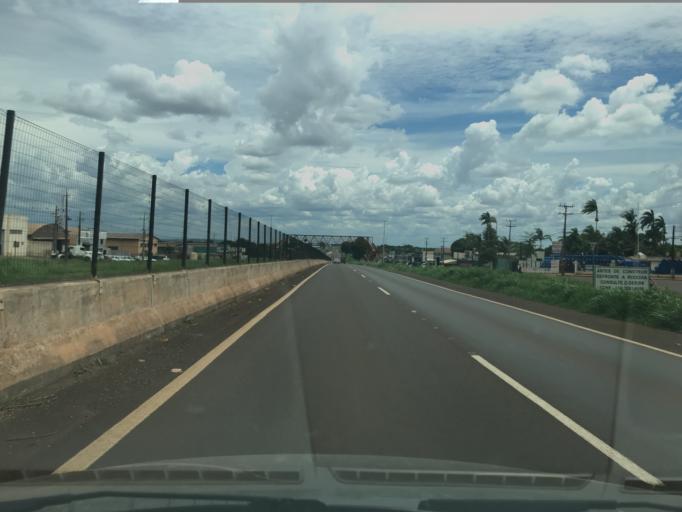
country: BR
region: Parana
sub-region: Paicandu
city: Paicandu
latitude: -23.4582
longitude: -52.0258
